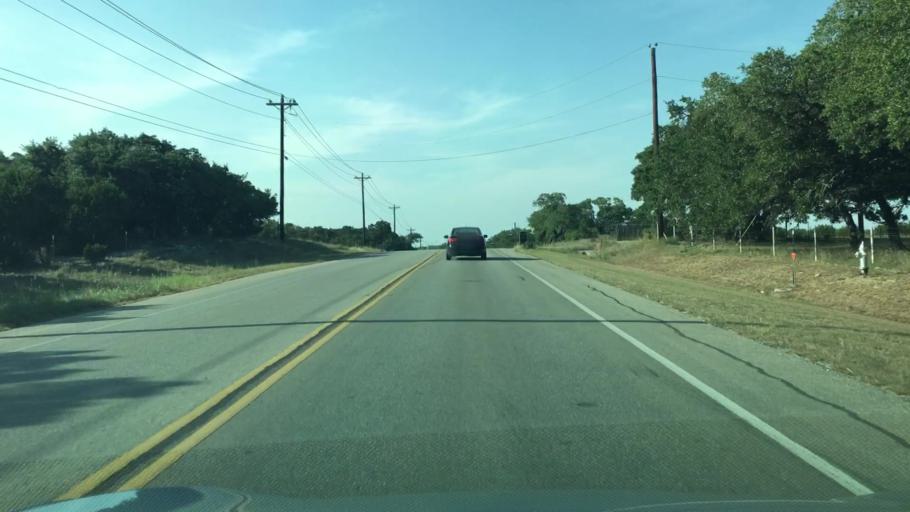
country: US
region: Texas
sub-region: Hays County
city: Dripping Springs
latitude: 30.1587
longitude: -98.0089
